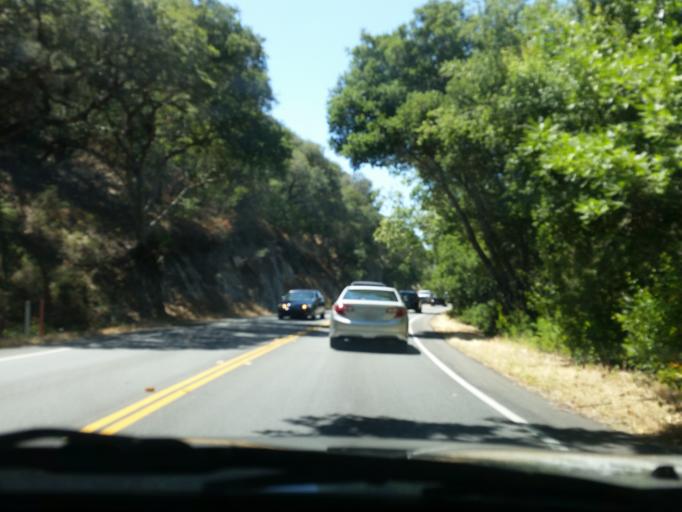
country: US
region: California
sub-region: San Luis Obispo County
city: Avila Beach
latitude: 35.1872
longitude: -120.7159
